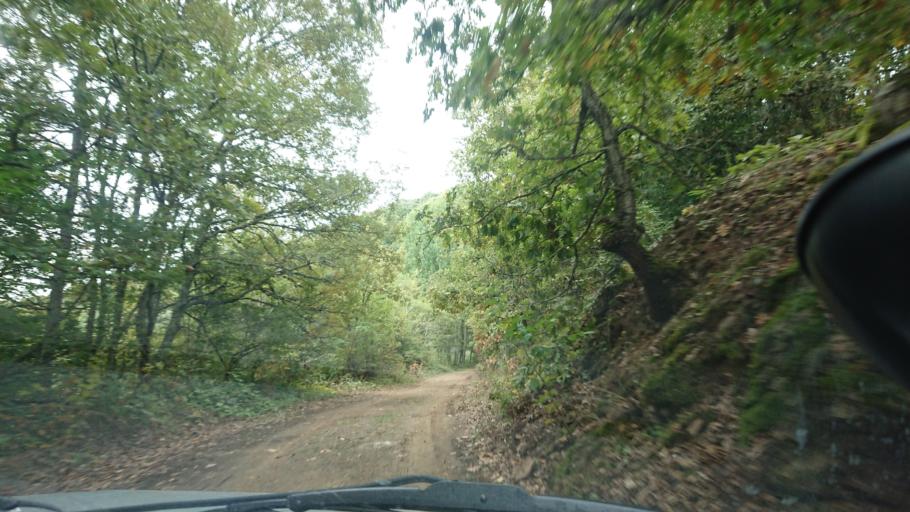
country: TR
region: Bilecik
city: Pazaryeri
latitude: 40.0187
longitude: 29.7895
